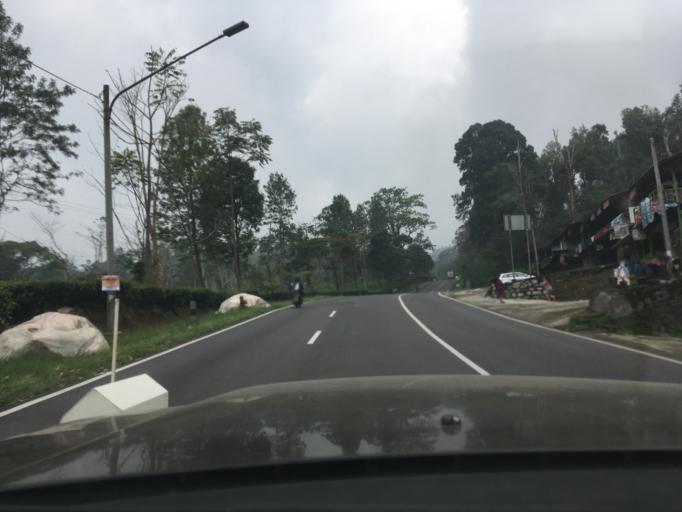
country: ID
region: West Java
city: Lembang
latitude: -6.7657
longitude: 107.6425
